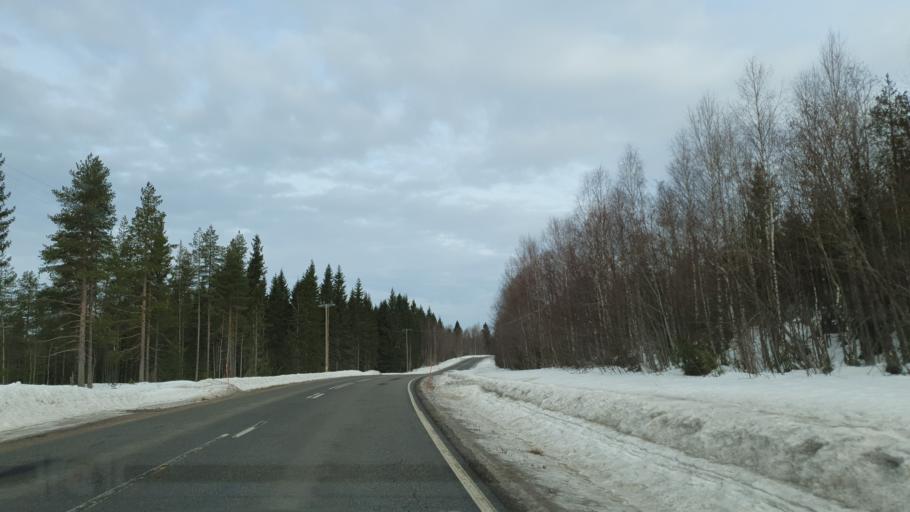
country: FI
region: Kainuu
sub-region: Kajaani
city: Paltamo
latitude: 64.2551
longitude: 28.0312
